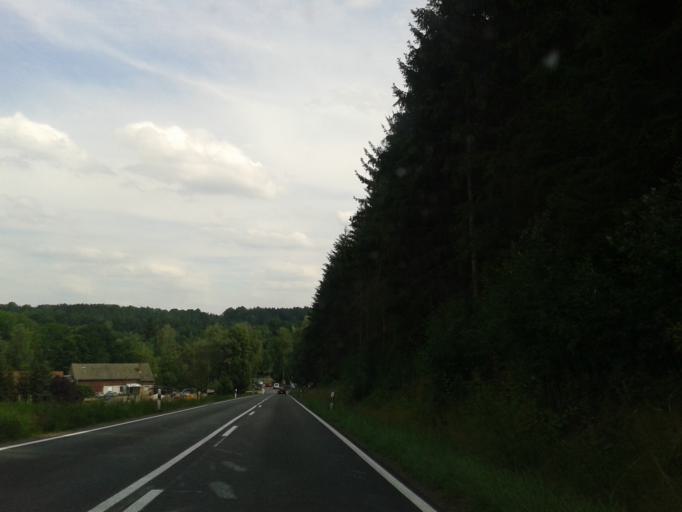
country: DE
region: Saxony
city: Reinsberg
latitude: 51.0213
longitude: 13.3361
